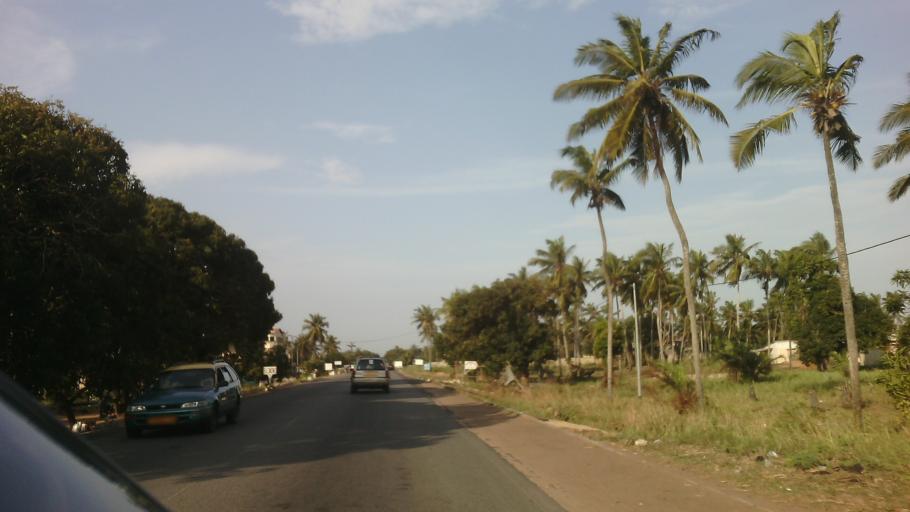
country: TG
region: Maritime
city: Vogan
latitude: 6.1951
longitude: 1.3998
